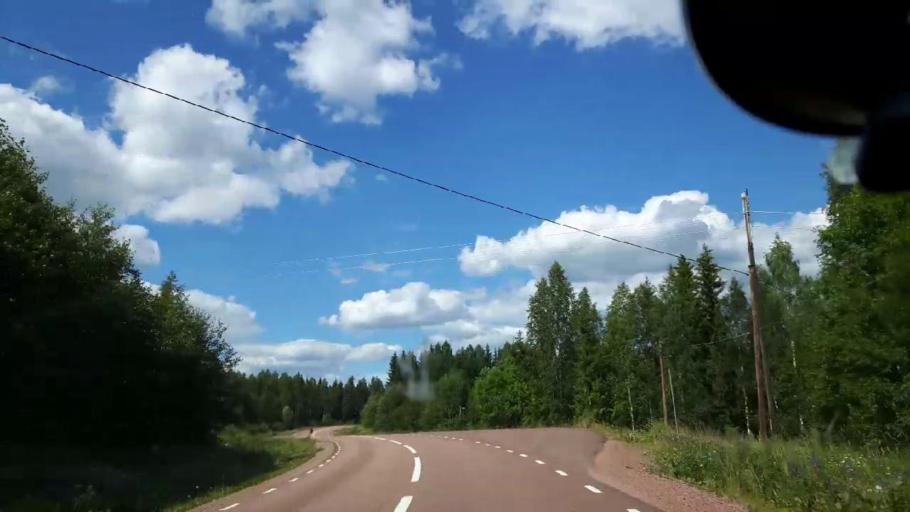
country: SE
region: Jaemtland
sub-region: Ragunda Kommun
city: Hammarstrand
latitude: 63.0278
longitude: 16.5280
